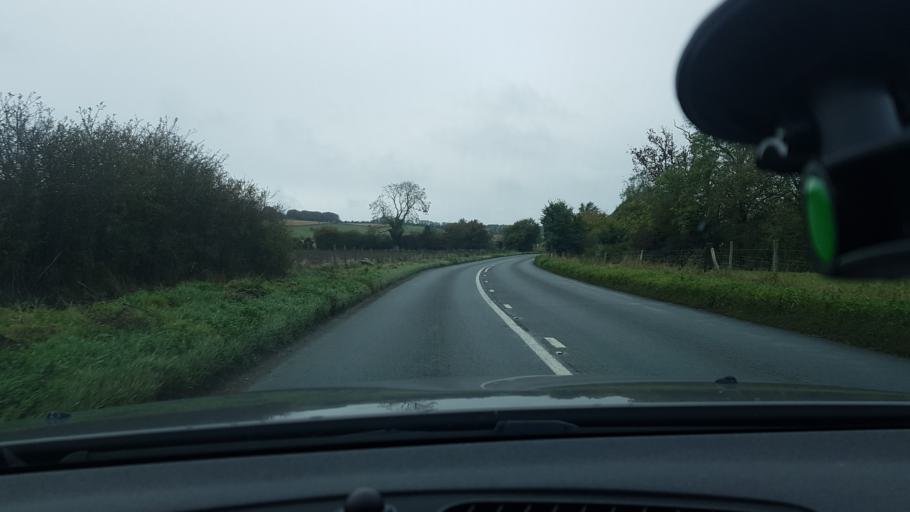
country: GB
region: England
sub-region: Wiltshire
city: Mildenhall
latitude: 51.4579
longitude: -1.7174
